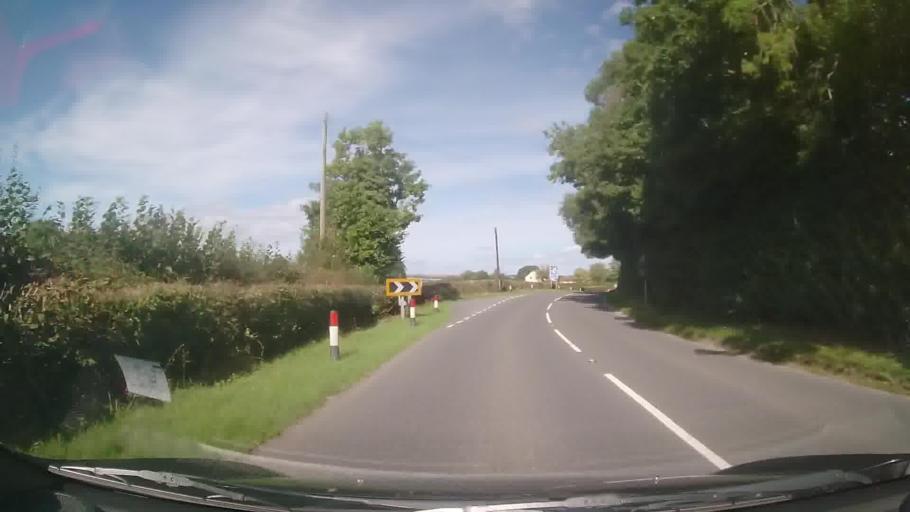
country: GB
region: England
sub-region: Herefordshire
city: Kington
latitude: 52.1763
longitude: -3.0322
